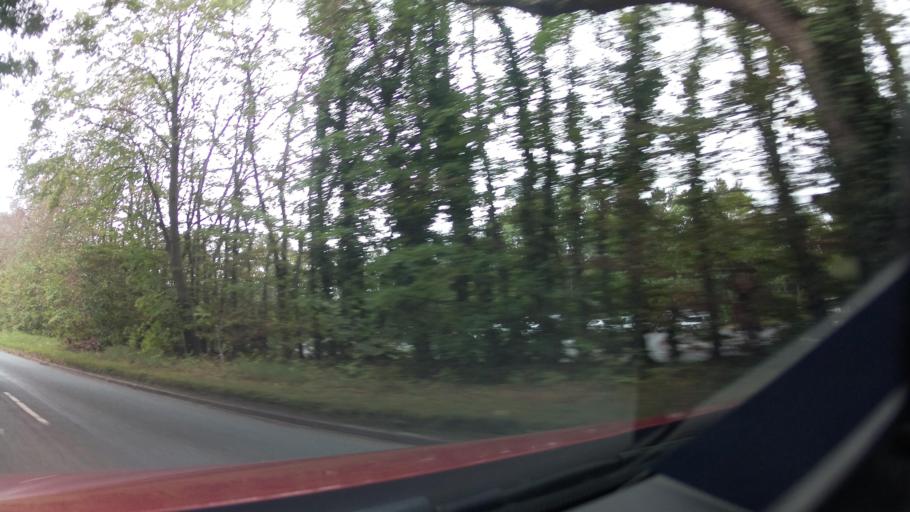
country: GB
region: England
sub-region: Staffordshire
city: Eccleshall
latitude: 52.8959
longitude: -2.2153
